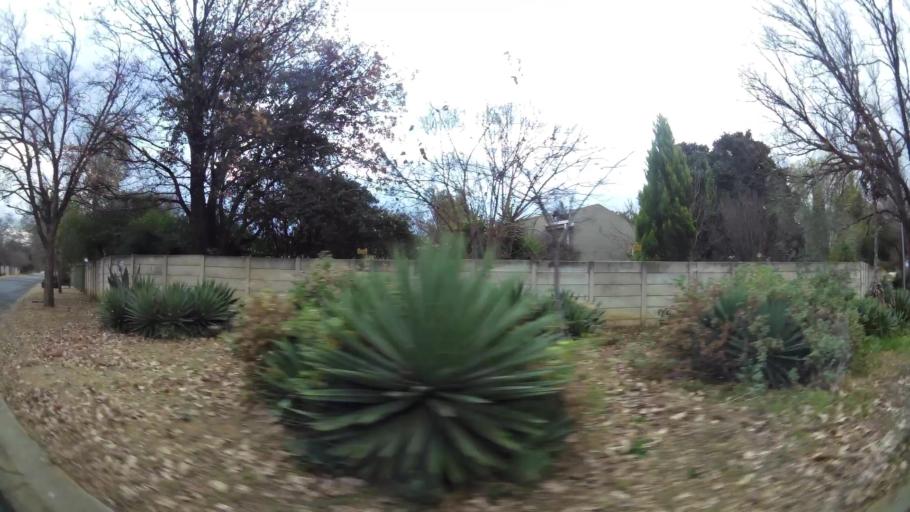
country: ZA
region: Orange Free State
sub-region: Lejweleputswa District Municipality
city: Welkom
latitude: -27.9550
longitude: 26.7410
